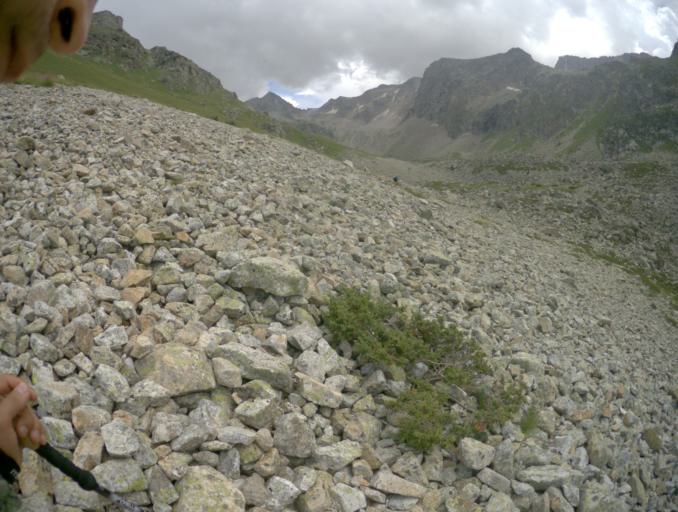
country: RU
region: Karachayevo-Cherkesiya
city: Uchkulan
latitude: 43.2909
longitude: 42.0802
